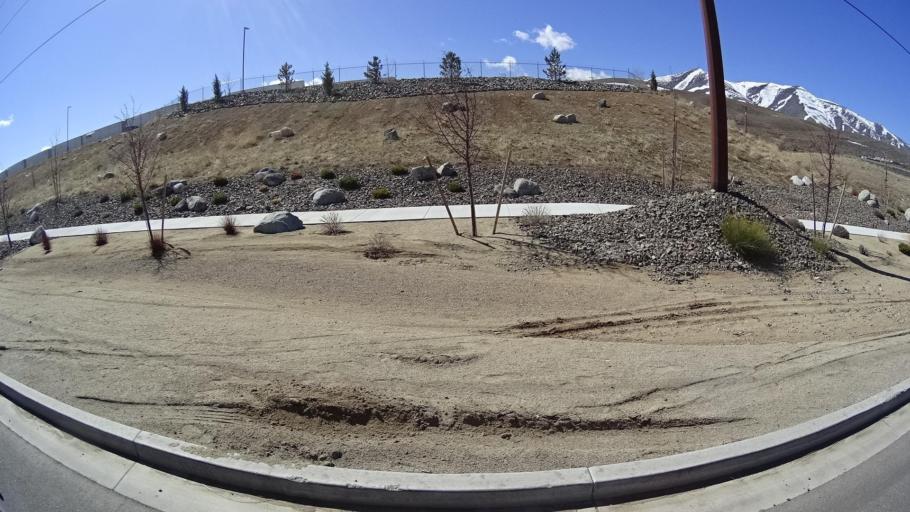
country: US
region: Nevada
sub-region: Washoe County
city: Lemmon Valley
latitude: 39.6070
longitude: -119.8793
